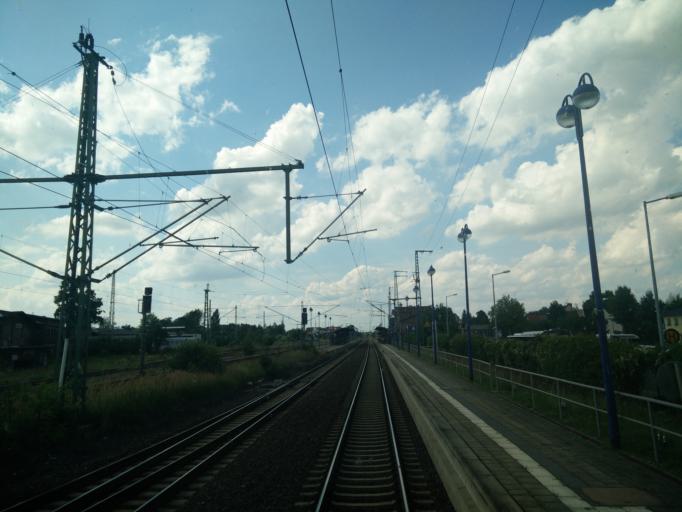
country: DE
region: Brandenburg
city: Lubbenau
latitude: 51.8611
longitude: 13.9635
